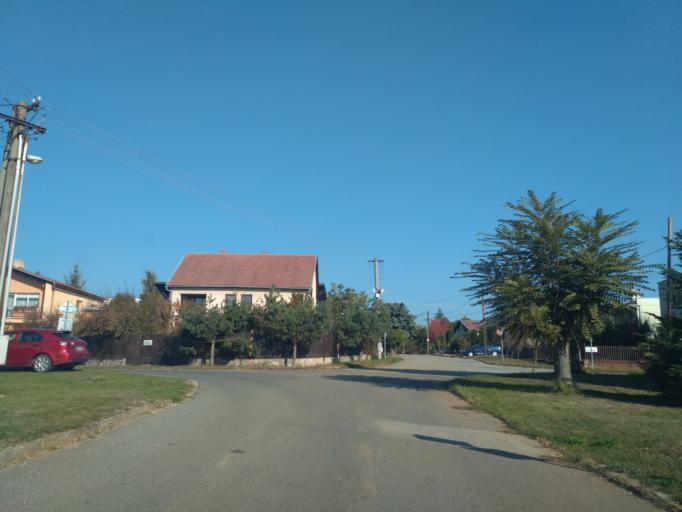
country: SK
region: Kosicky
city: Moldava nad Bodvou
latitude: 48.6162
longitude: 20.9892
